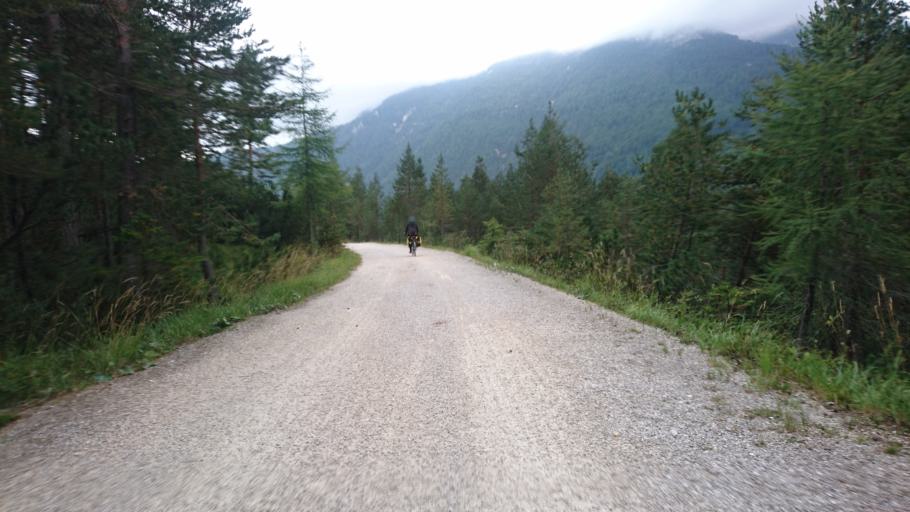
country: IT
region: Veneto
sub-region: Provincia di Belluno
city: Cortina d'Ampezzo
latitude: 46.5876
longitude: 12.1160
